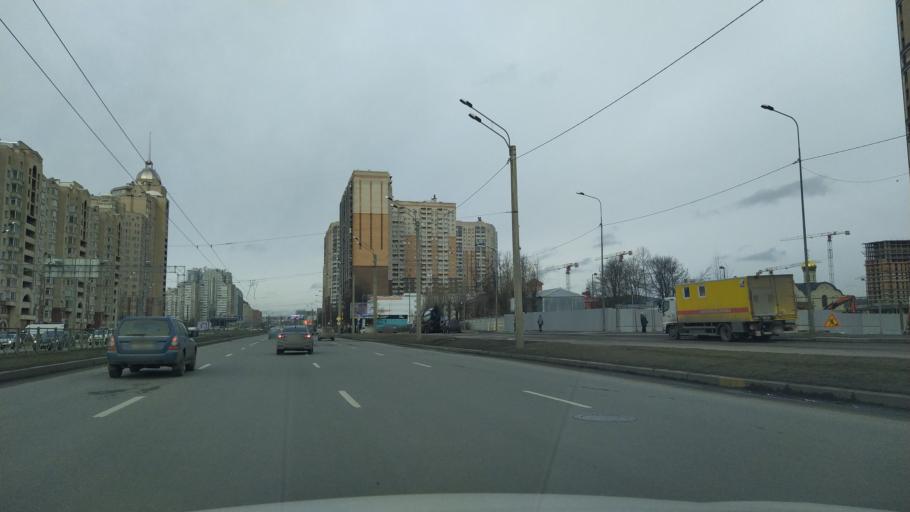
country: RU
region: Leningrad
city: Chernaya Rechka
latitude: 59.9966
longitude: 30.3003
